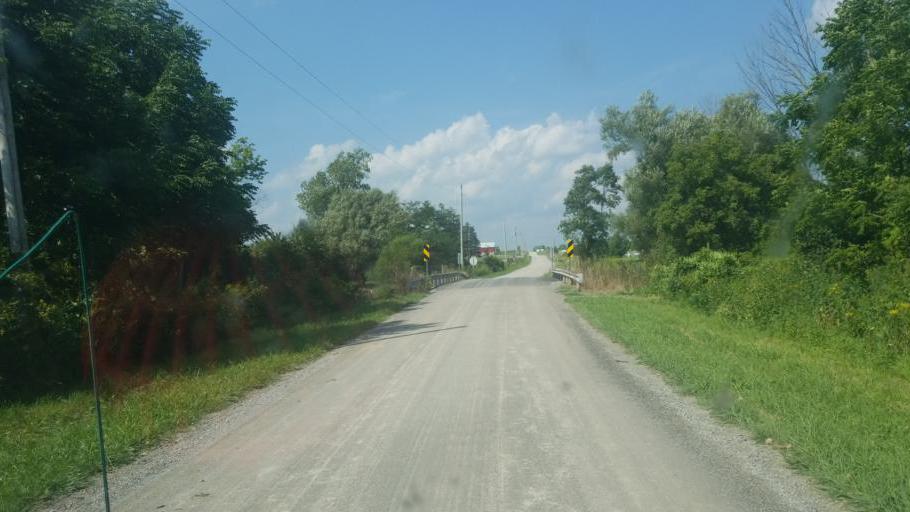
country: US
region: Ohio
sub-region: Wayne County
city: West Salem
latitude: 41.0445
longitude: -82.1449
